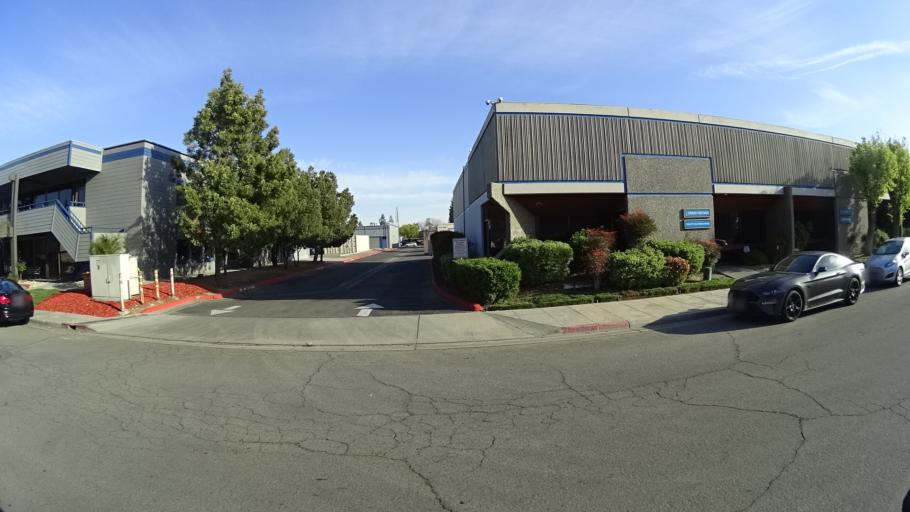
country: US
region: California
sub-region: Fresno County
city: West Park
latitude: 36.8054
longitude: -119.8668
